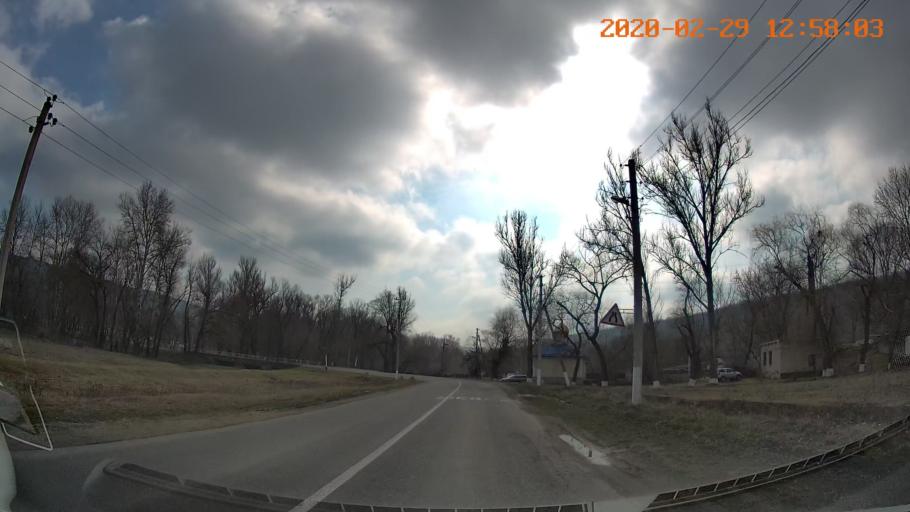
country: MD
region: Telenesti
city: Camenca
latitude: 48.0718
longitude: 28.7177
